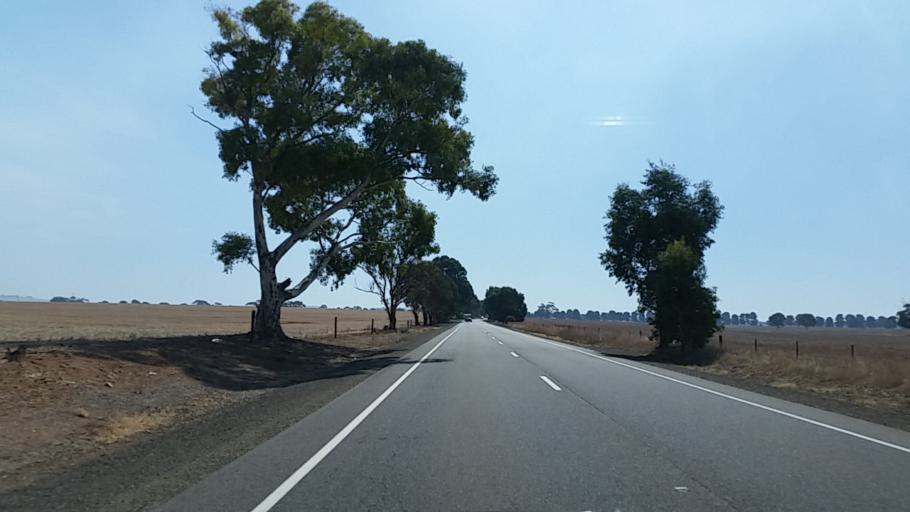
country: AU
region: South Australia
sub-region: Light
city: Kapunda
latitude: -34.2443
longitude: 138.7469
